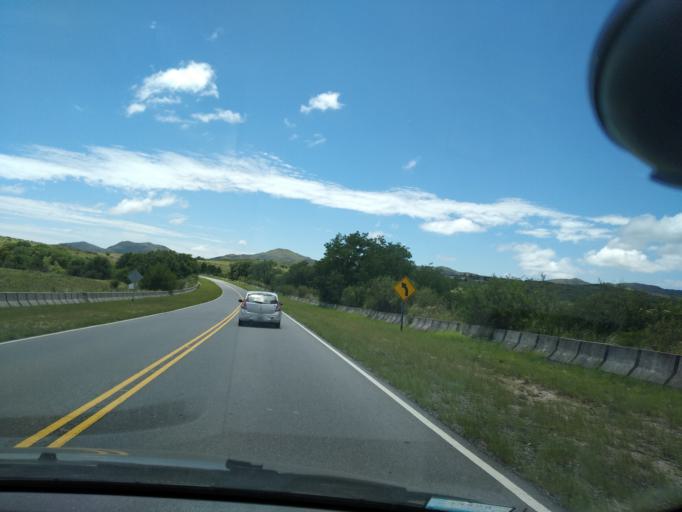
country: AR
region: Cordoba
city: Cuesta Blanca
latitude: -31.5759
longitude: -64.5966
